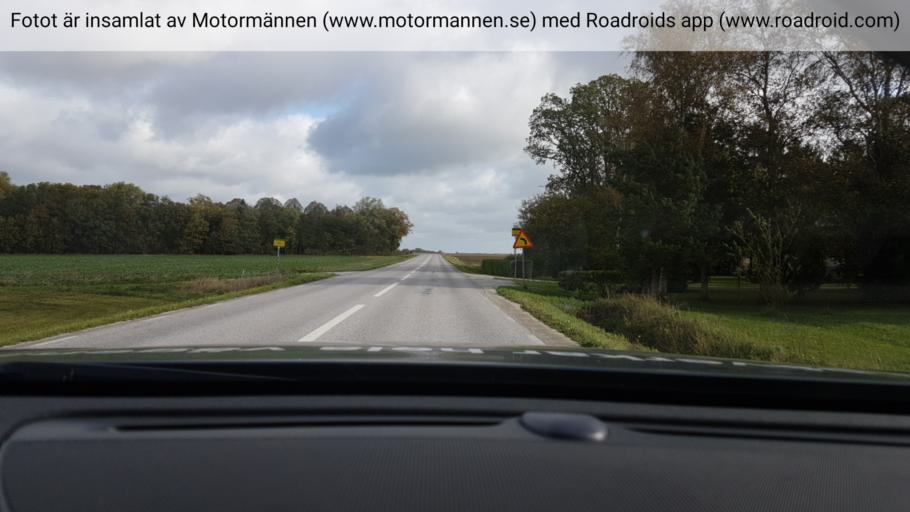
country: SE
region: Gotland
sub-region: Gotland
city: Visby
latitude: 57.6954
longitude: 18.5054
